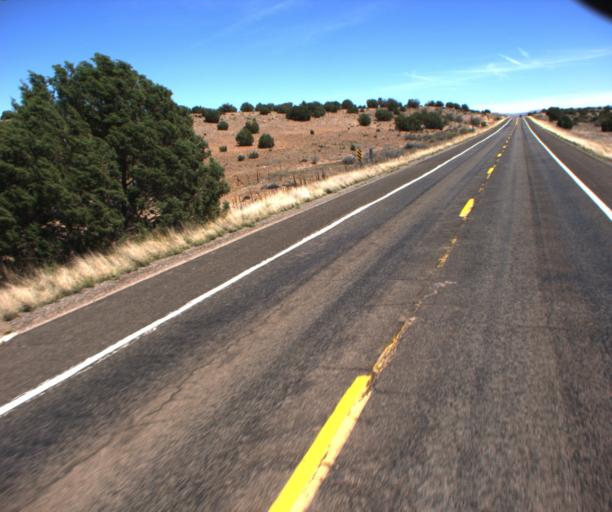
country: US
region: Arizona
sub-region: Mohave County
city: Peach Springs
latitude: 35.4562
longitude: -113.6224
